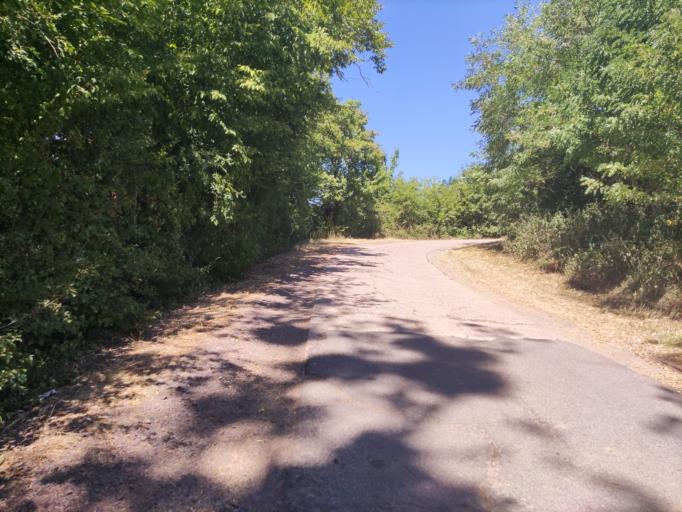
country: FR
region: Lorraine
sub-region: Departement de la Moselle
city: Bouzonville
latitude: 49.3442
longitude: 6.5947
